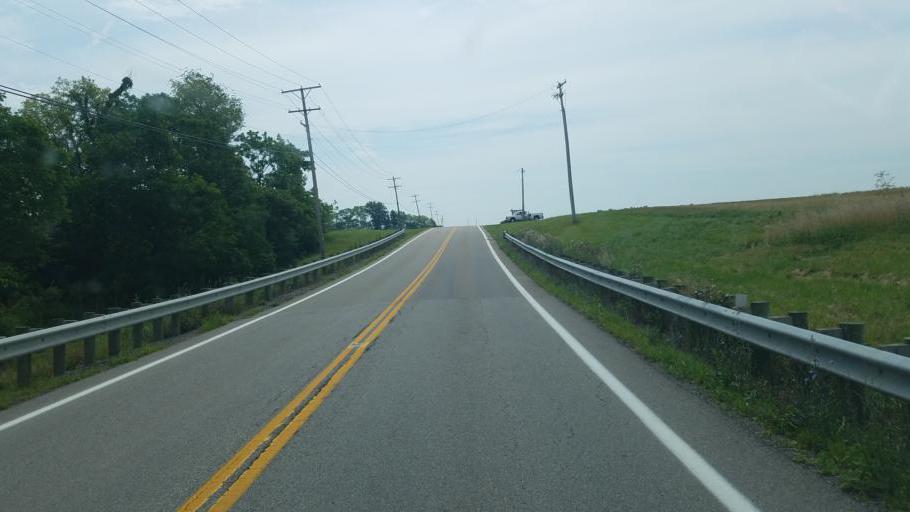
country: US
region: Ohio
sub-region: Madison County
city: West Jefferson
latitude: 39.9734
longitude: -83.3747
